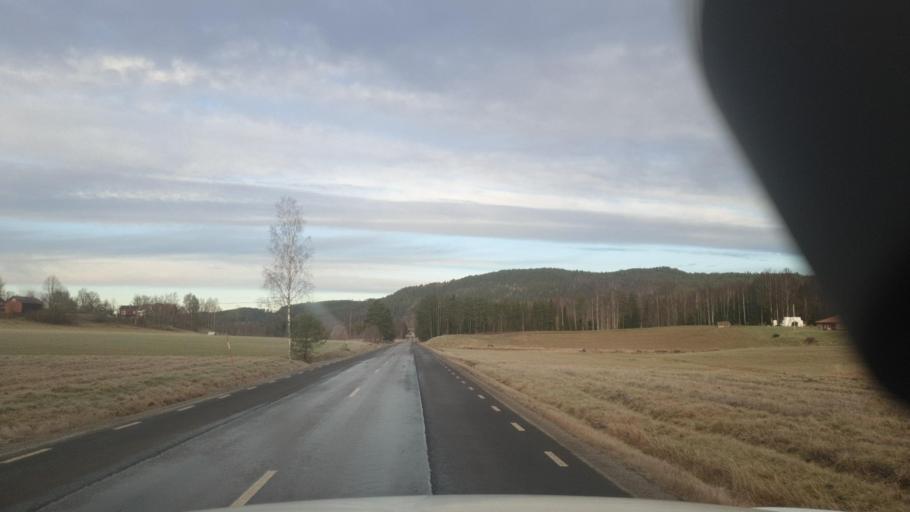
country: SE
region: Vaermland
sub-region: Arvika Kommun
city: Arvika
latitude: 59.7375
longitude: 12.6414
